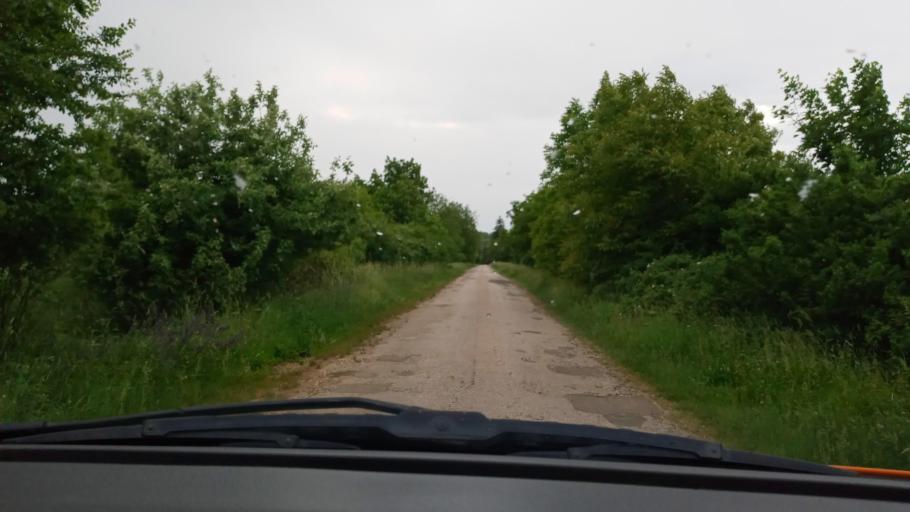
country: HU
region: Baranya
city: Harkany
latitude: 45.9033
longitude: 18.1376
